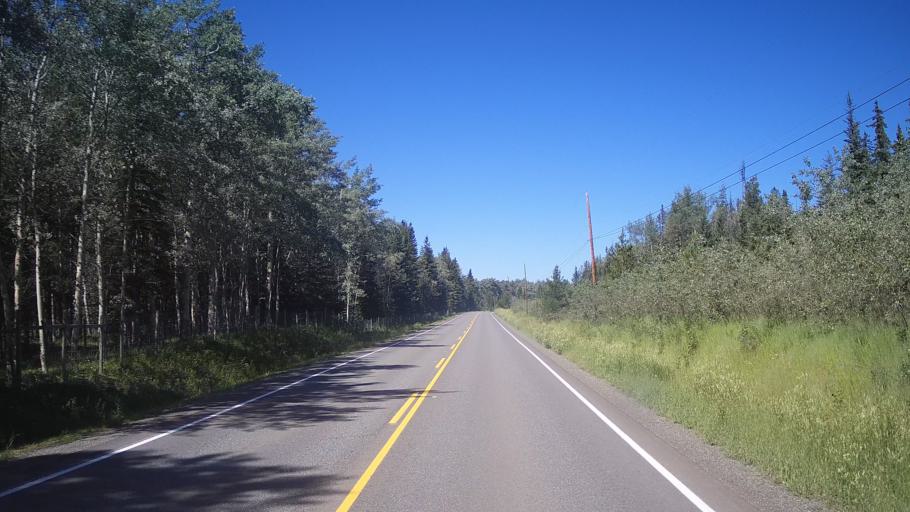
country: CA
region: British Columbia
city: Cache Creek
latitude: 51.5402
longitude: -121.0444
